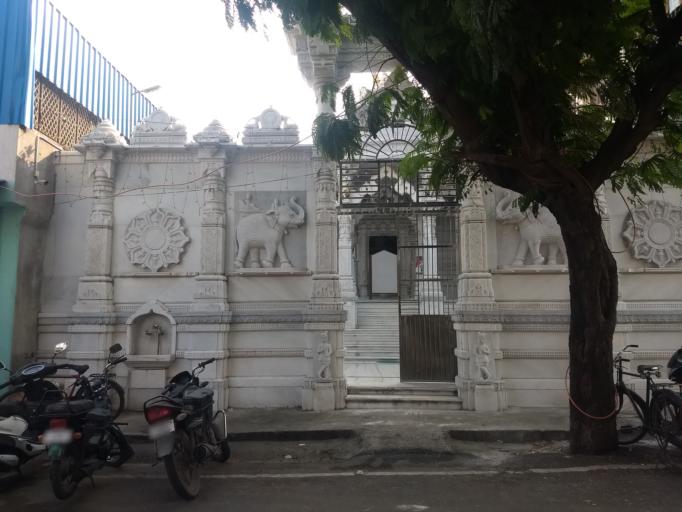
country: IN
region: Tamil Nadu
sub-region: Kancheepuram
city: Pallavaram
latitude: 12.9303
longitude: 80.1161
